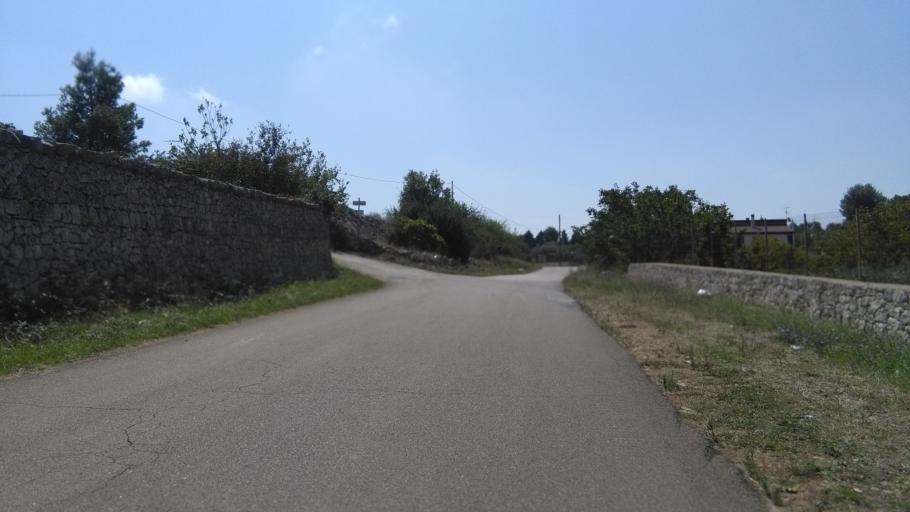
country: IT
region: Apulia
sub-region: Provincia di Bari
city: Putignano
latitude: 40.8275
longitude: 17.1348
